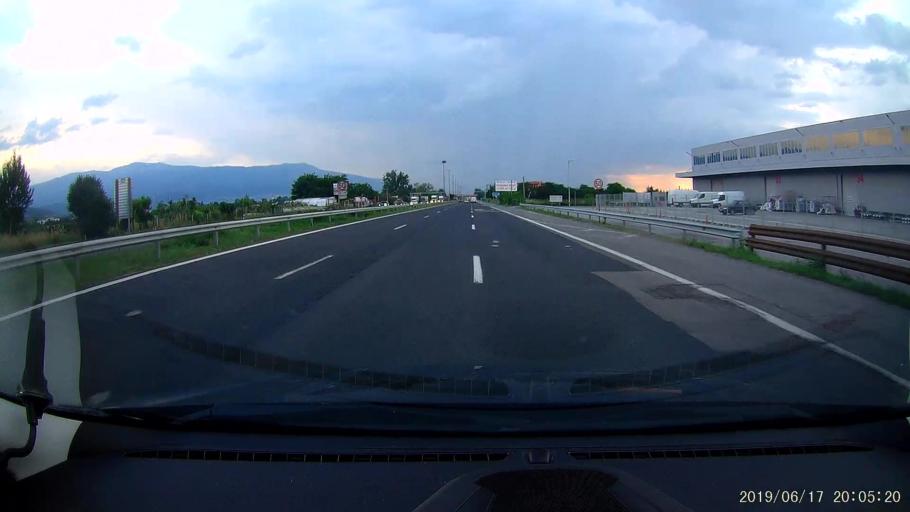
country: BG
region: Sofiya
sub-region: Obshtina Elin Pelin
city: Elin Pelin
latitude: 42.6321
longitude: 23.4571
